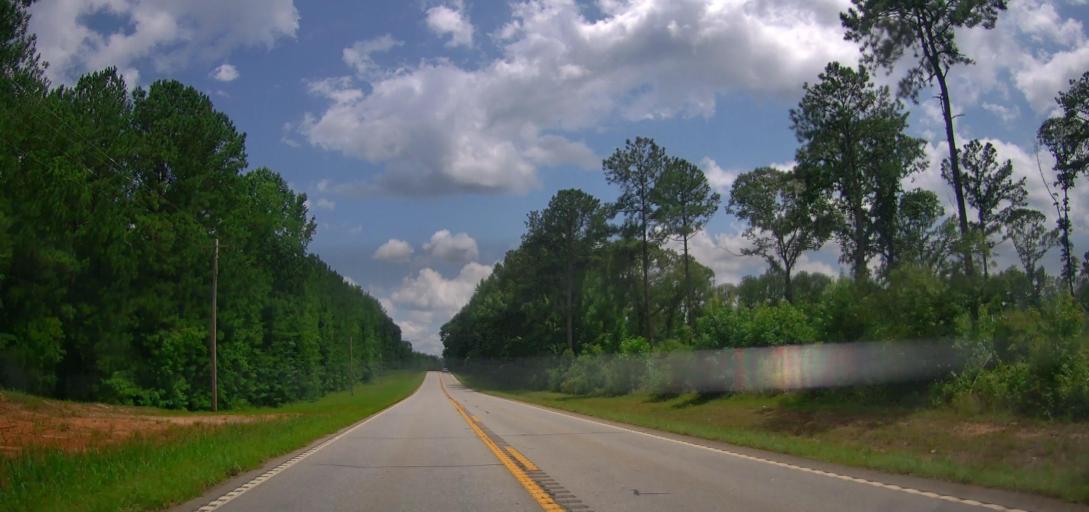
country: US
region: Georgia
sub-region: Heard County
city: Franklin
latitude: 33.3088
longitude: -85.1405
